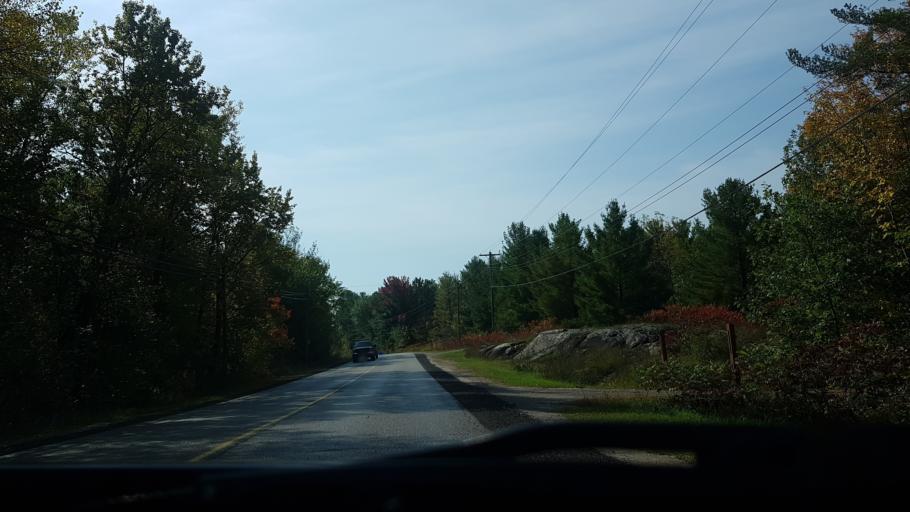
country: CA
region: Ontario
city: Gravenhurst
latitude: 44.7596
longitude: -79.3324
